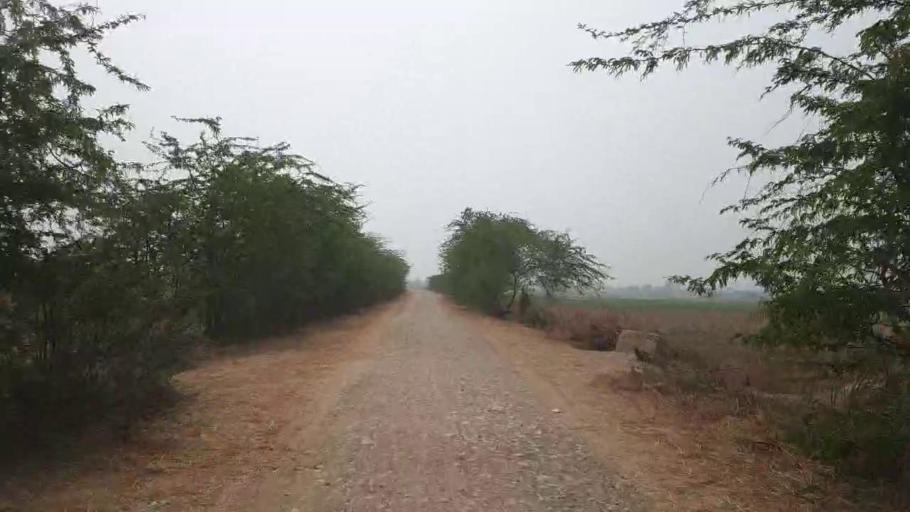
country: PK
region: Sindh
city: Kario
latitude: 24.6500
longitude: 68.6404
